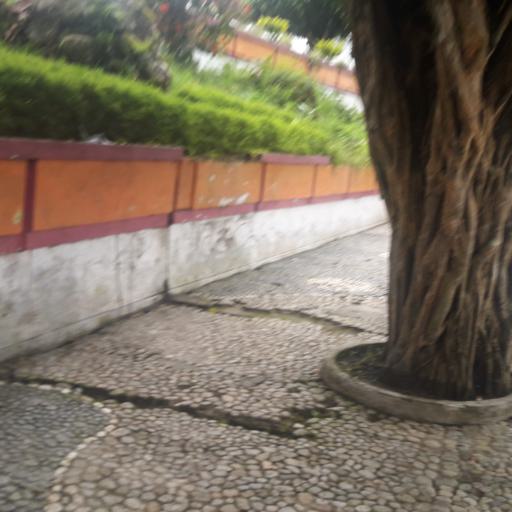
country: EC
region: Napo
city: Tena
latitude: -0.9910
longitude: -77.8153
